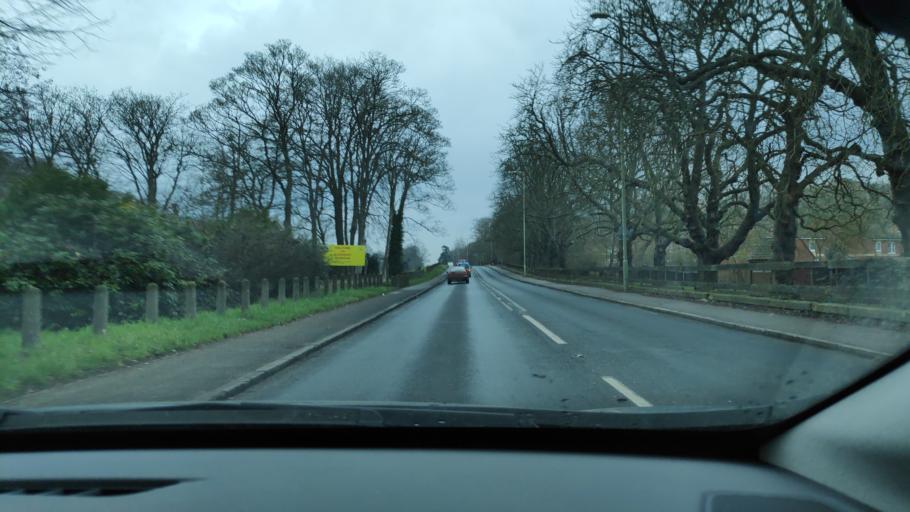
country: GB
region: England
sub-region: Hampshire
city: Aldershot
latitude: 51.2524
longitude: -0.7761
